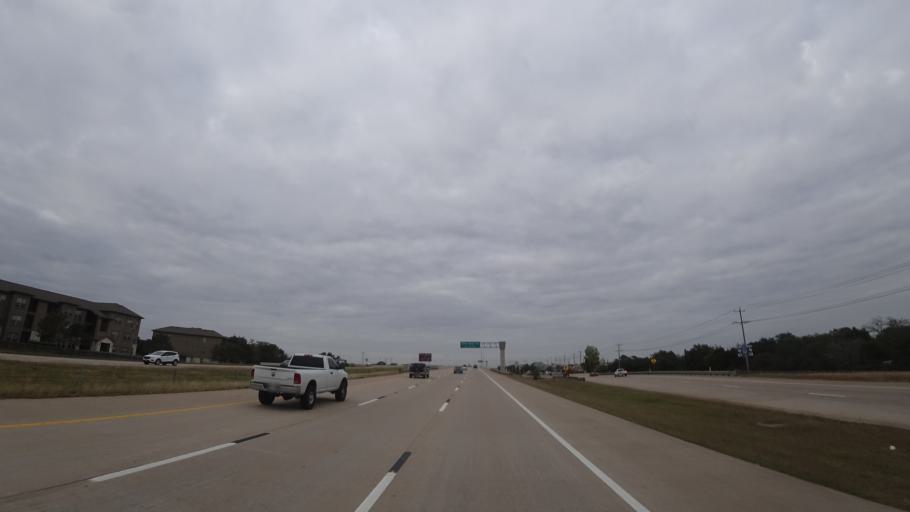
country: US
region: Texas
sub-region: Williamson County
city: Cedar Park
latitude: 30.5218
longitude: -97.8154
